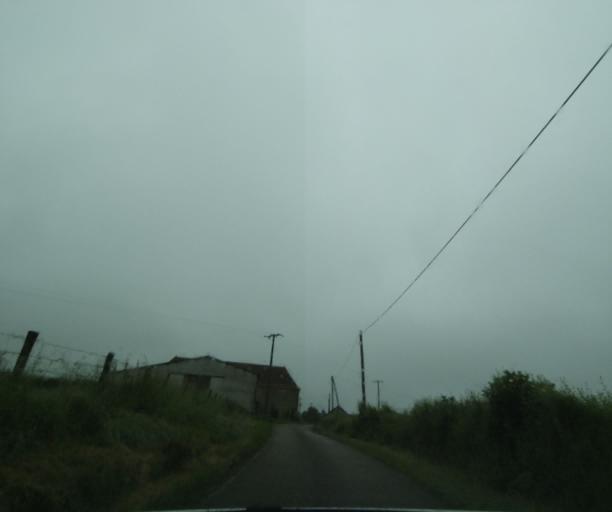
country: FR
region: Bourgogne
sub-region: Departement de Saone-et-Loire
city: Charolles
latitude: 46.3987
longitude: 4.2134
